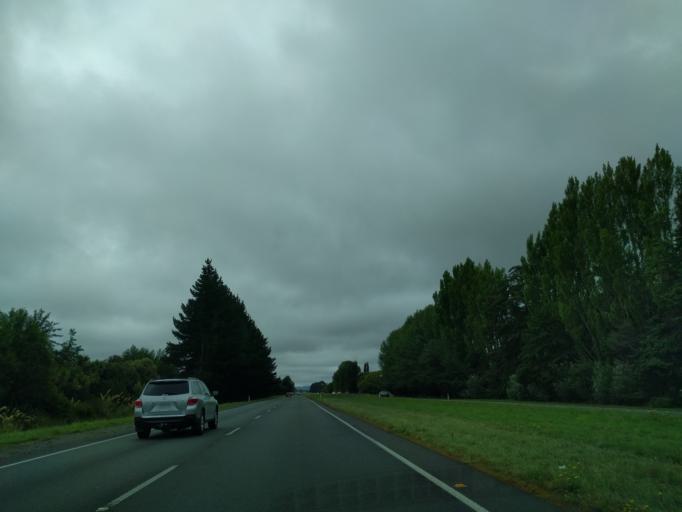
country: NZ
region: Canterbury
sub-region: Waimakariri District
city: Kaiapoi
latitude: -43.3943
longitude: 172.6407
